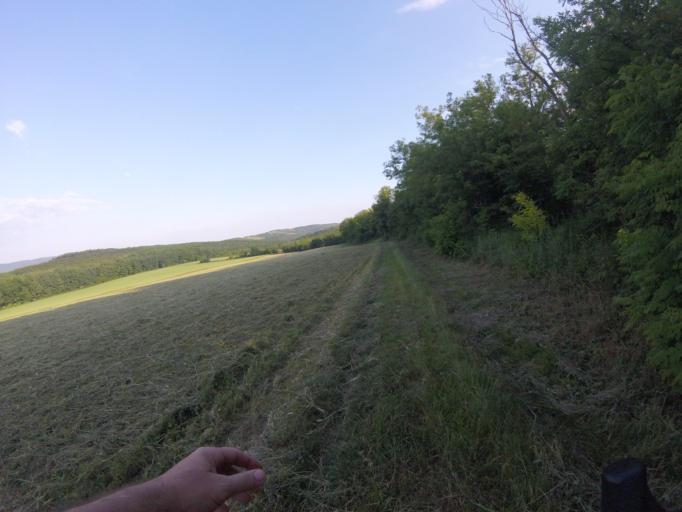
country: HU
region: Zala
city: Zalaszentgrot
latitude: 46.8814
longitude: 17.1330
